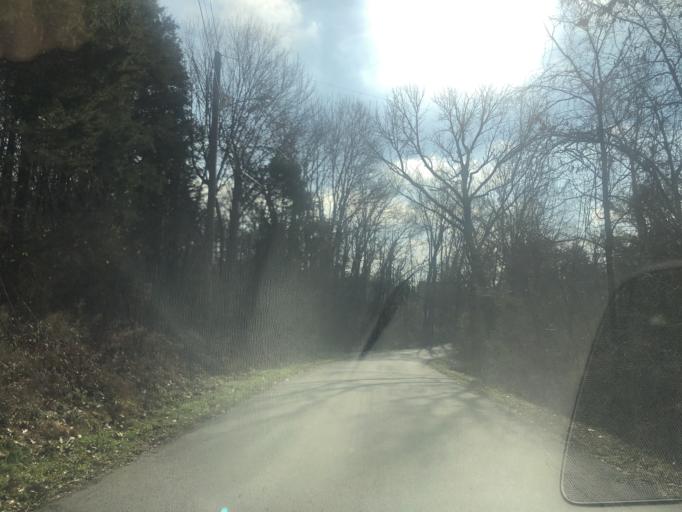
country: US
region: Tennessee
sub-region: Rutherford County
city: La Vergne
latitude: 36.0619
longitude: -86.6534
